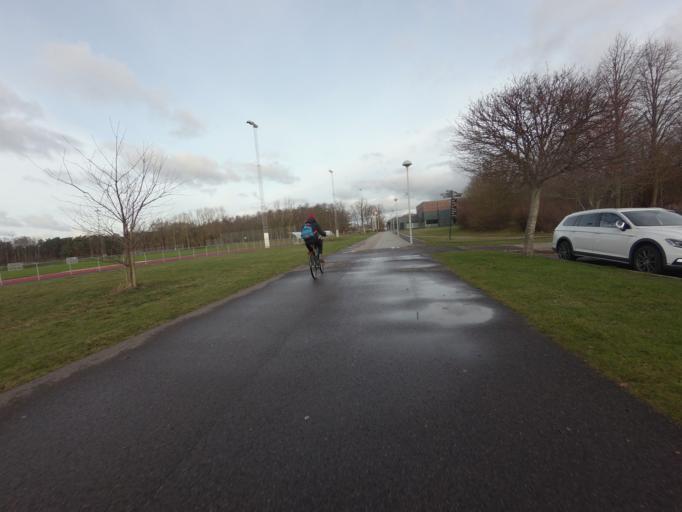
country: SE
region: Skane
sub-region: Hoganas Kommun
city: Hoganas
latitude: 56.1840
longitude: 12.5664
